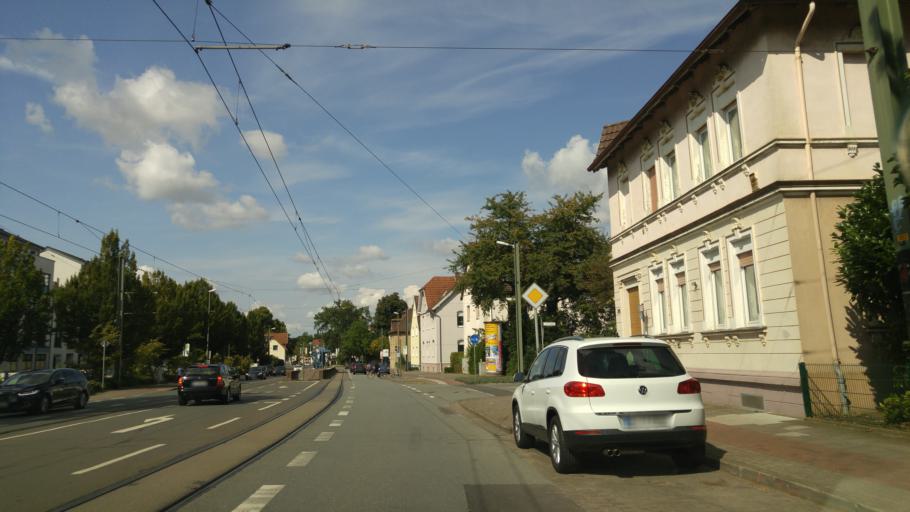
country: DE
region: North Rhine-Westphalia
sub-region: Regierungsbezirk Detmold
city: Bielefeld
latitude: 52.0485
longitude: 8.5221
